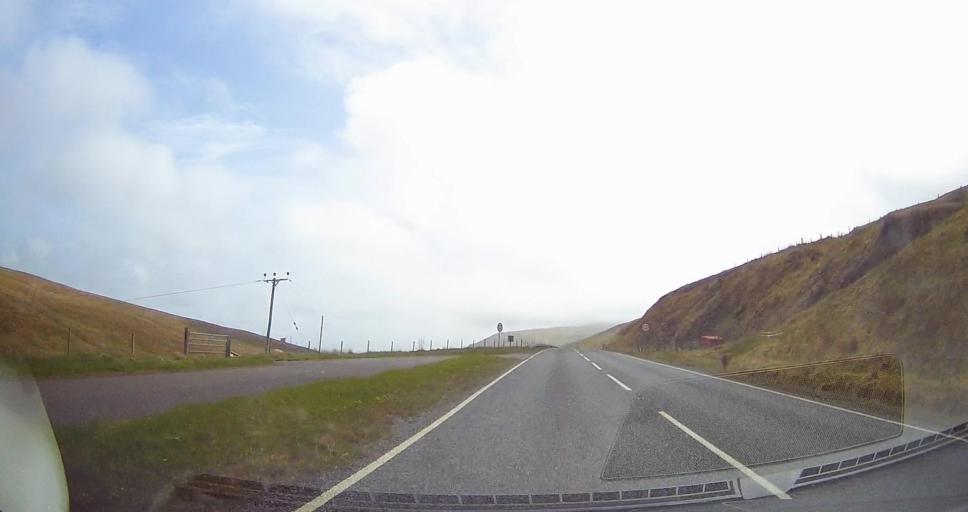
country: GB
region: Scotland
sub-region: Shetland Islands
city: Sandwick
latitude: 60.0024
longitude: -1.2797
